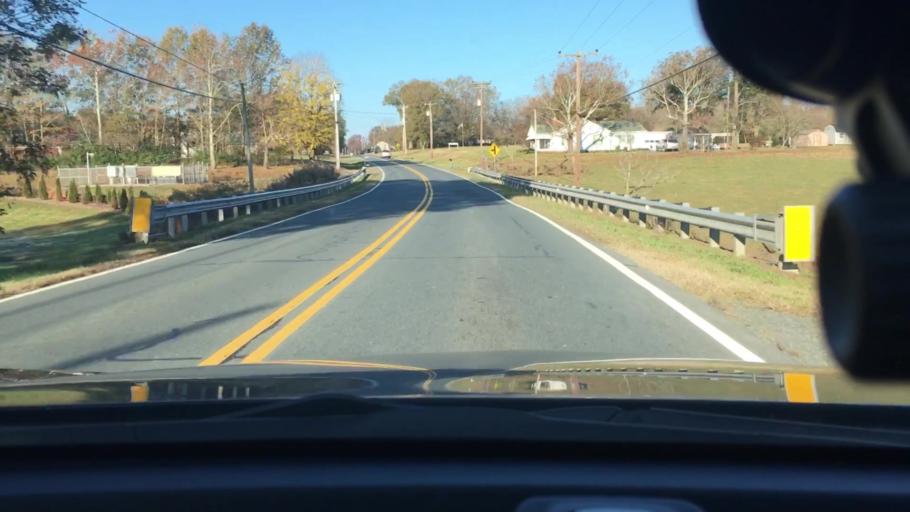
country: US
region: North Carolina
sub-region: Stanly County
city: Albemarle
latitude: 35.3692
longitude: -80.2736
